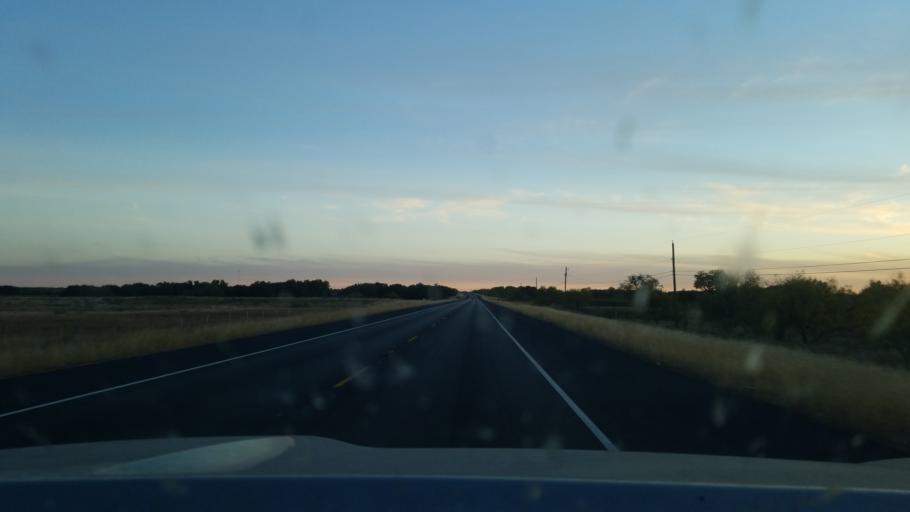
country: US
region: Texas
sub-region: Stephens County
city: Breckenridge
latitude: 32.6543
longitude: -98.9025
